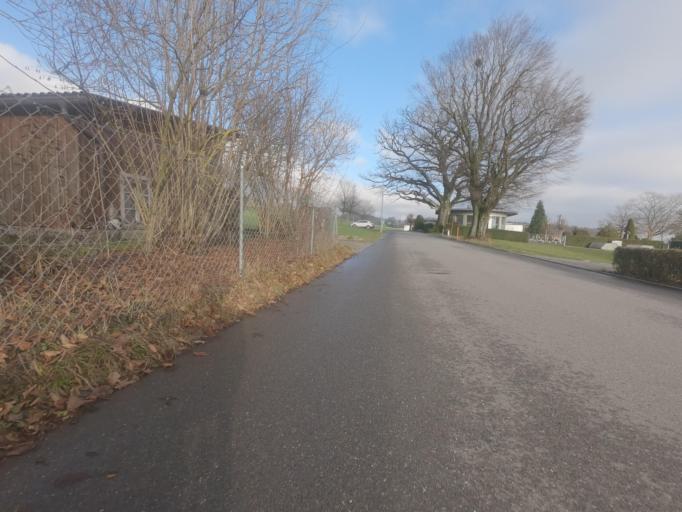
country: CH
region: Solothurn
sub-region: Bezirk Lebern
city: Bettlach
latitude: 47.2013
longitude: 7.4291
